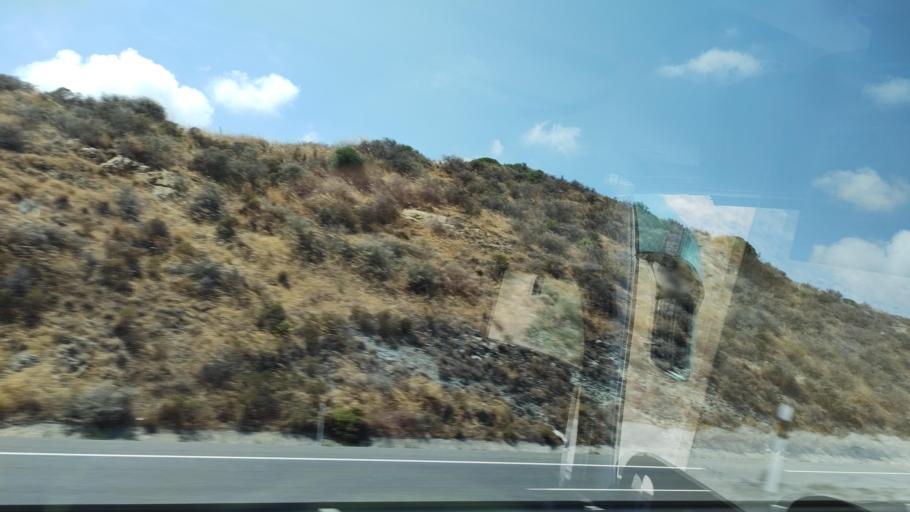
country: ES
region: Andalusia
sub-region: Provincia de Malaga
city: Manilva
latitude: 36.3608
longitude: -5.2680
